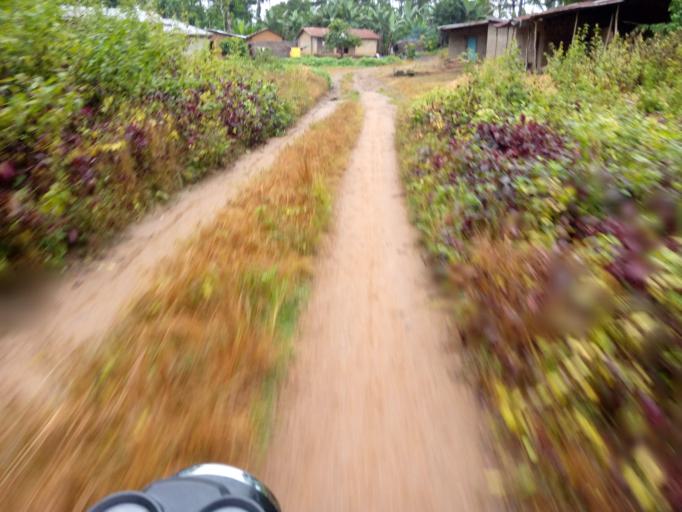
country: SL
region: Eastern Province
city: Buedu
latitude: 8.4704
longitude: -10.3483
